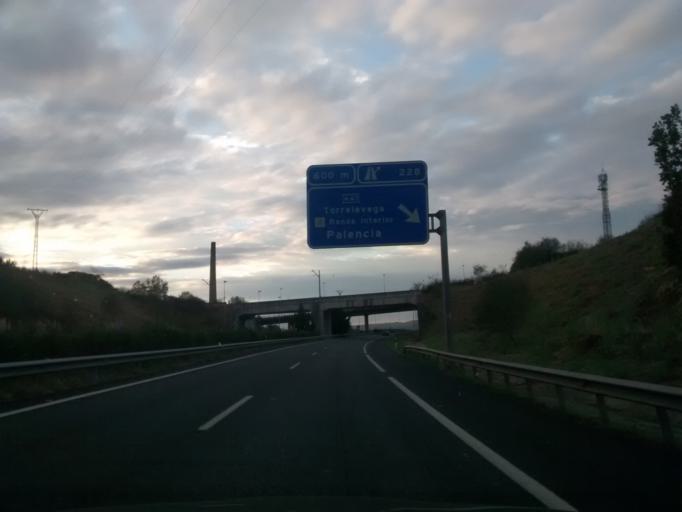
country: ES
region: Cantabria
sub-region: Provincia de Cantabria
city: Torrelavega
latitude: 43.3447
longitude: -4.0210
